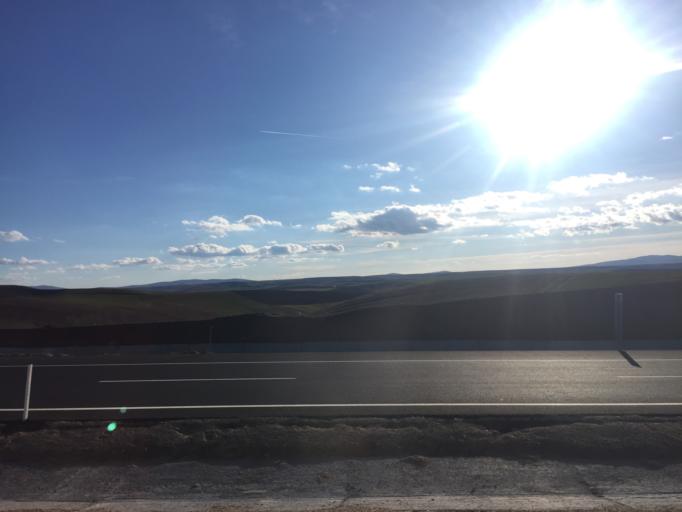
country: TR
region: Kirsehir
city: Kaman
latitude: 39.5146
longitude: 33.7727
